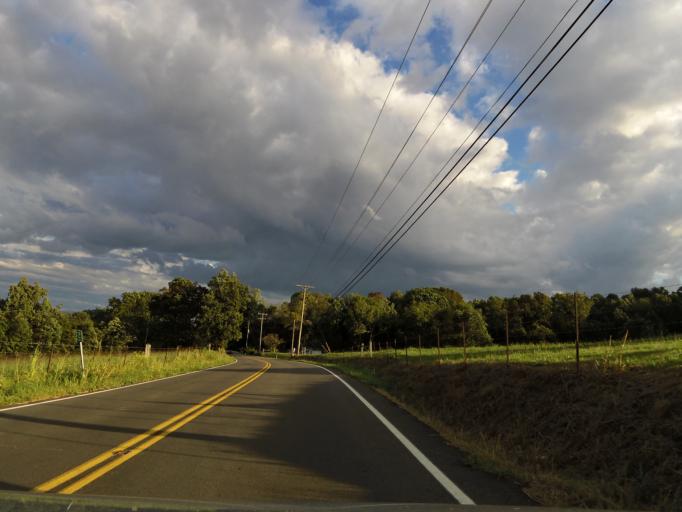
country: US
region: Tennessee
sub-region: Jefferson County
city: Jefferson City
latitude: 36.1949
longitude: -83.4994
